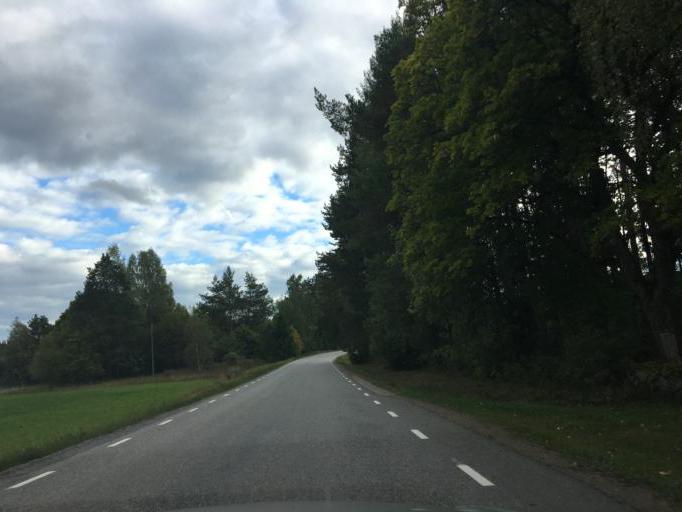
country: SE
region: Vaestmanland
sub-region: Vasteras
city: Tillberga
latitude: 59.5906
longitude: 16.7057
